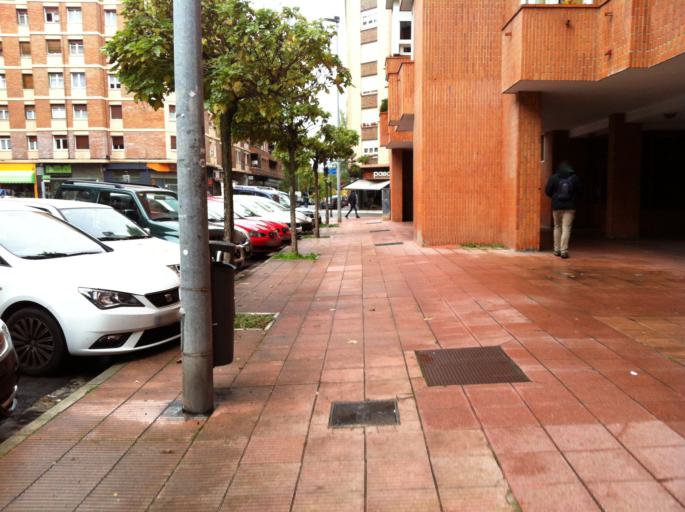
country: ES
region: Basque Country
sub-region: Provincia de Alava
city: Gasteiz / Vitoria
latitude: 42.8501
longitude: -2.6850
